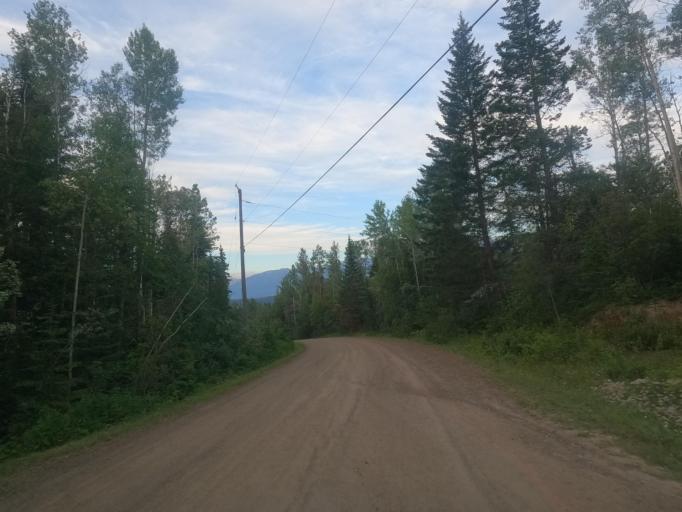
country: CA
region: British Columbia
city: Golden
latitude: 51.4490
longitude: -117.0068
